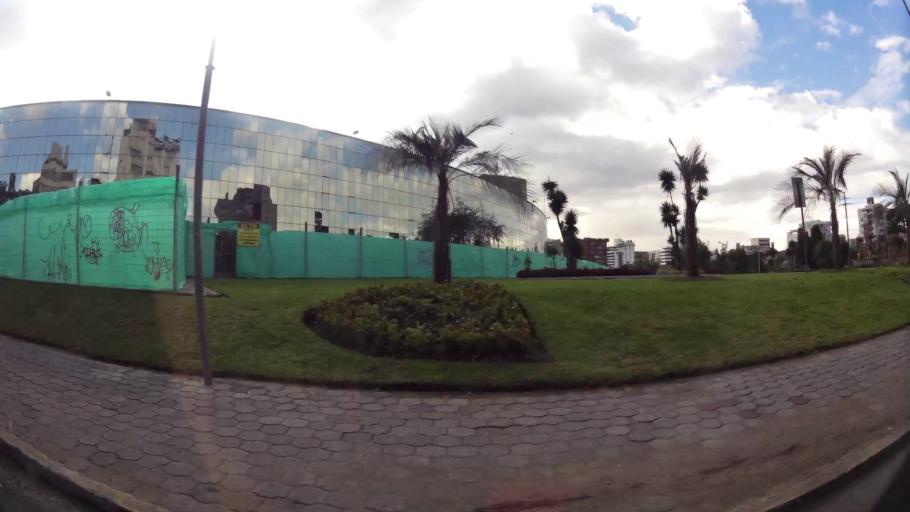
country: EC
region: Pichincha
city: Quito
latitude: -0.2107
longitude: -78.4946
